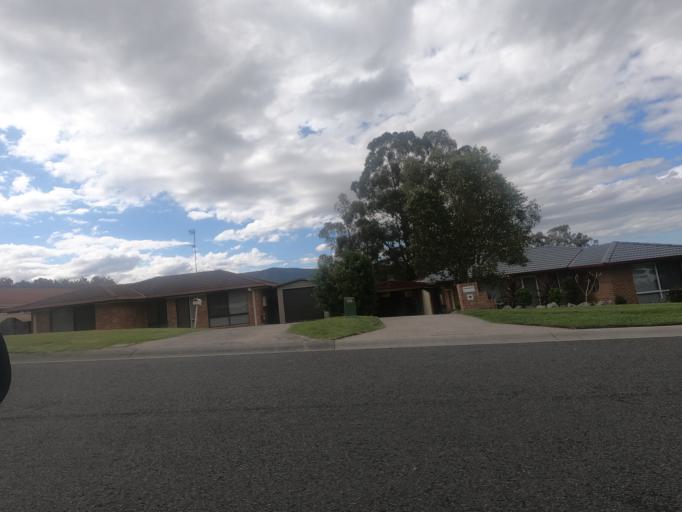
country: AU
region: New South Wales
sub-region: Wollongong
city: Dapto
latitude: -34.4914
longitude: 150.7754
